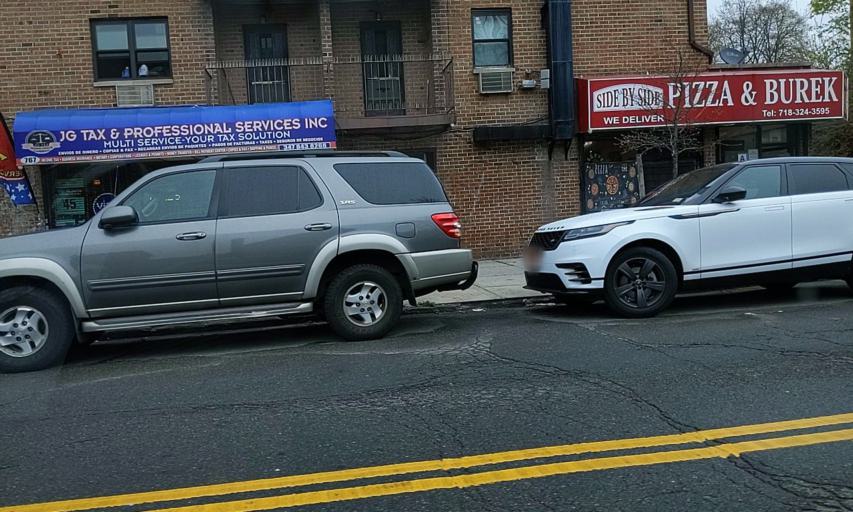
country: US
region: New York
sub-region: Bronx
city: The Bronx
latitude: 40.8596
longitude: -73.8649
